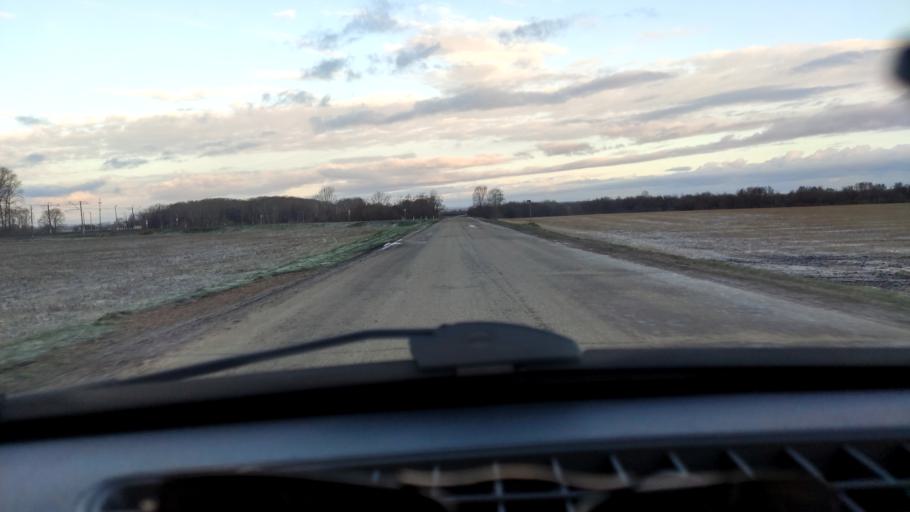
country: RU
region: Bashkortostan
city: Kabakovo
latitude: 54.4716
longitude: 56.2132
